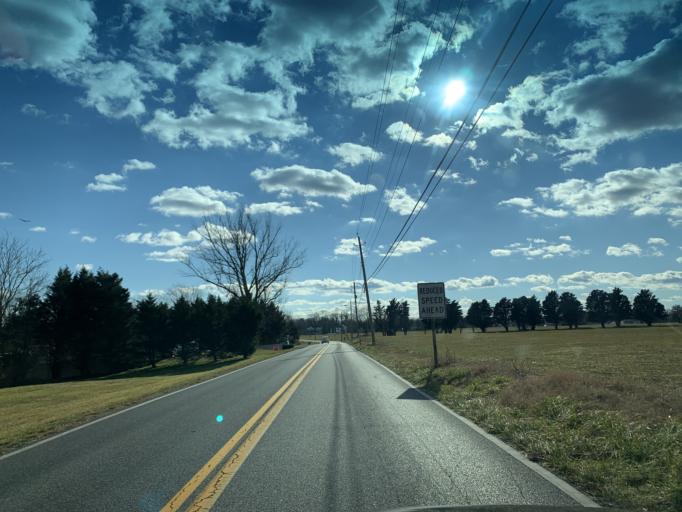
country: US
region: Maryland
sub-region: Worcester County
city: Berlin
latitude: 38.3382
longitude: -75.2202
